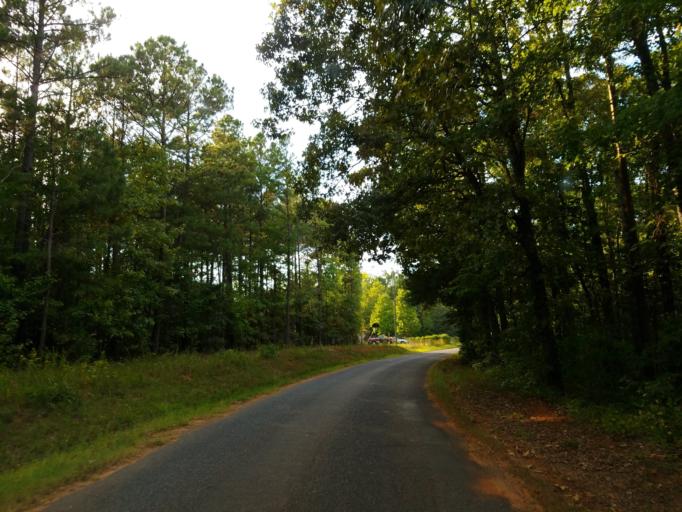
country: US
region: Georgia
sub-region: Monroe County
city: Forsyth
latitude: 33.1304
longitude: -84.0228
